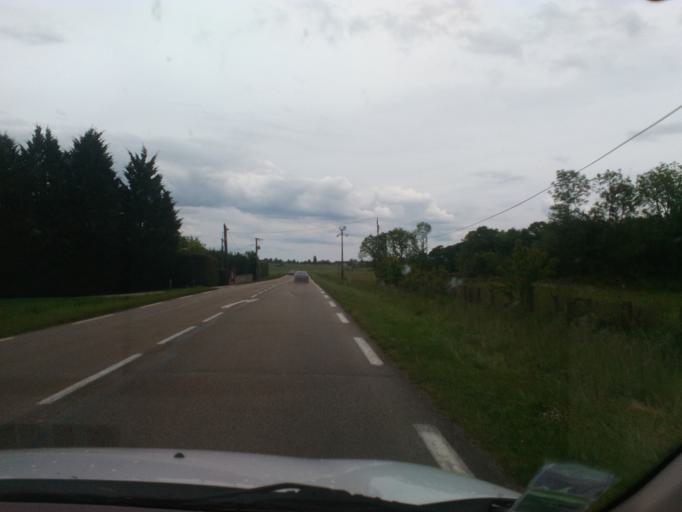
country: FR
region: Champagne-Ardenne
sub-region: Departement de l'Aube
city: Lusigny-sur-Barse
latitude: 48.2420
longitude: 4.3642
